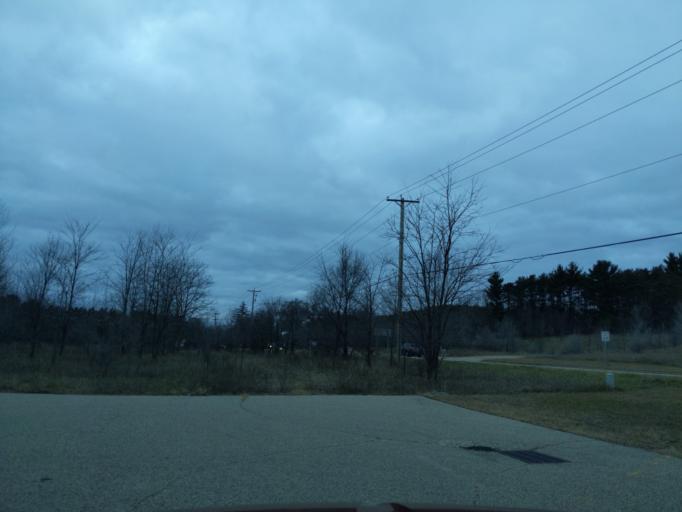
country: US
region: Wisconsin
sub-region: Waushara County
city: Wautoma
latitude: 44.0772
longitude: -89.2995
